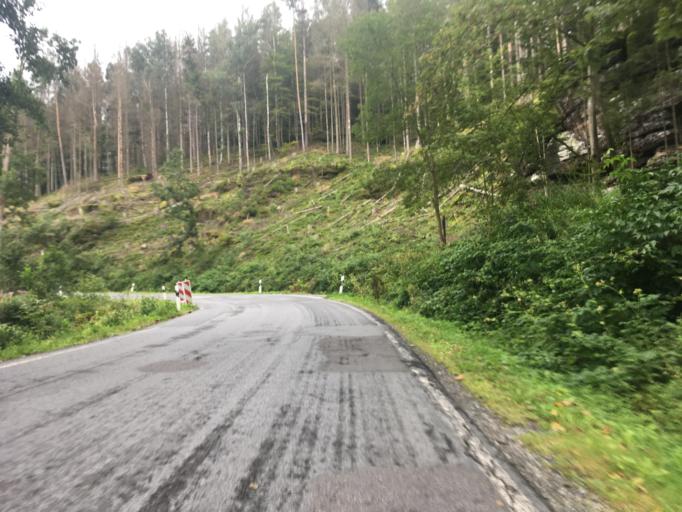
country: DE
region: Saxony
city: Sebnitz
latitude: 50.9277
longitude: 14.3096
